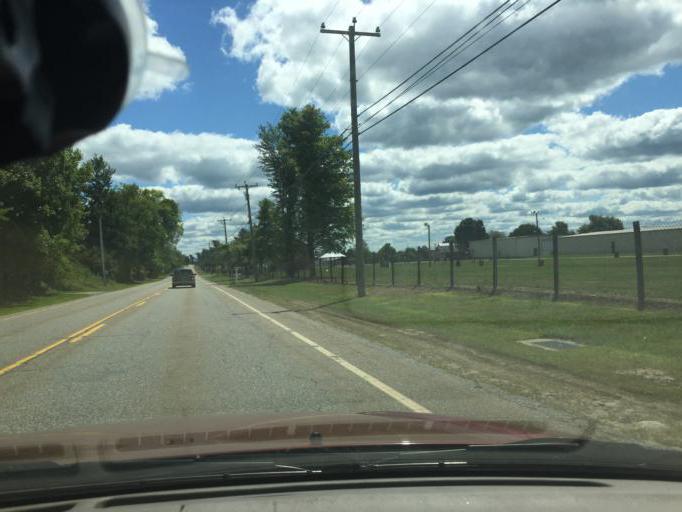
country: US
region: Connecticut
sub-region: Litchfield County
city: West Torrington
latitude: 41.8262
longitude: -73.2226
